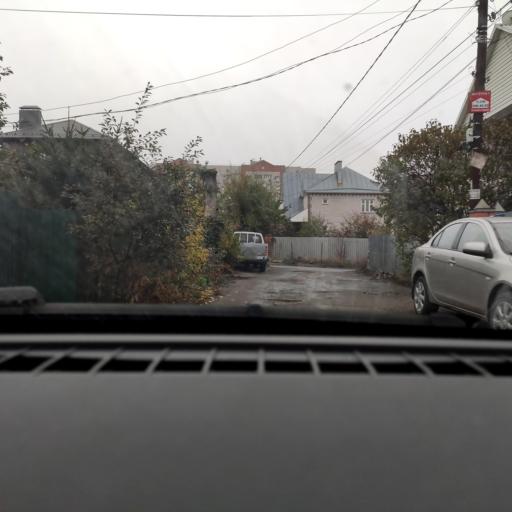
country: RU
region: Voronezj
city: Voronezh
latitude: 51.6677
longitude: 39.2868
